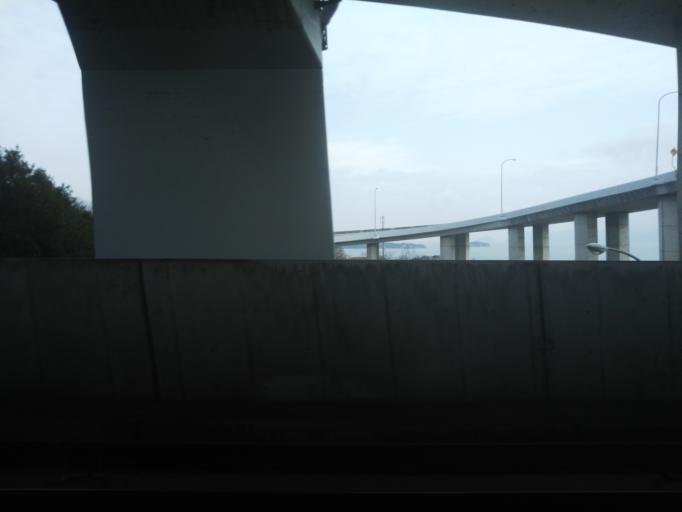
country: JP
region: Kagawa
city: Sakaidecho
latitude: 34.4216
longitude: 133.8038
